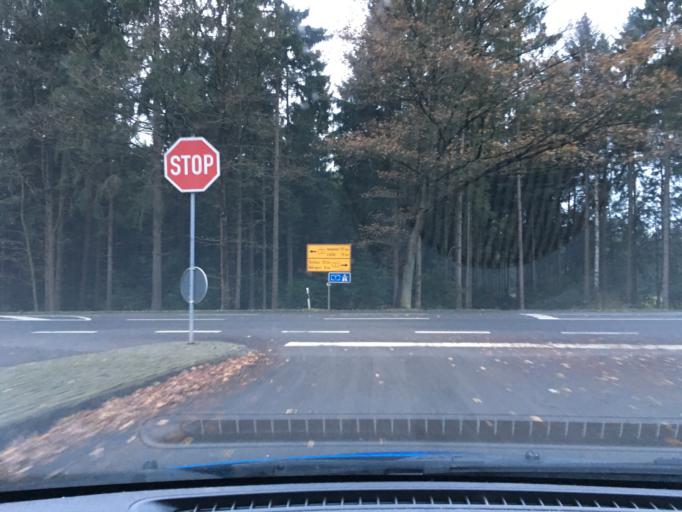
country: DE
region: Lower Saxony
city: Bergen
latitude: 52.7323
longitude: 9.9750
